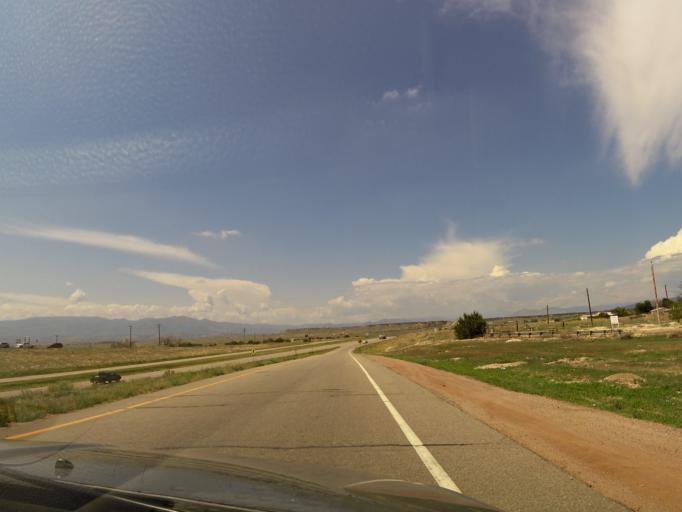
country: US
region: Colorado
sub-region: Fremont County
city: Penrose
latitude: 38.4192
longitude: -105.0414
